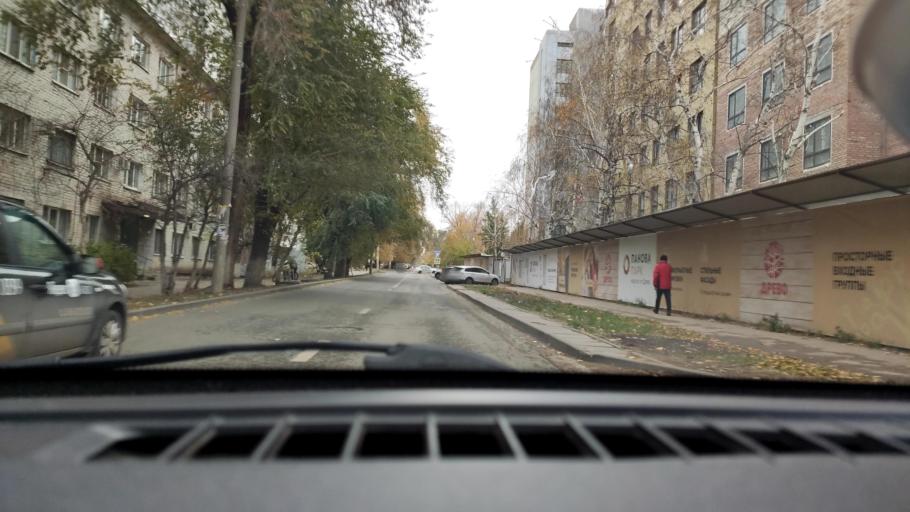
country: RU
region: Samara
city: Samara
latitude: 53.2111
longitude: 50.1605
